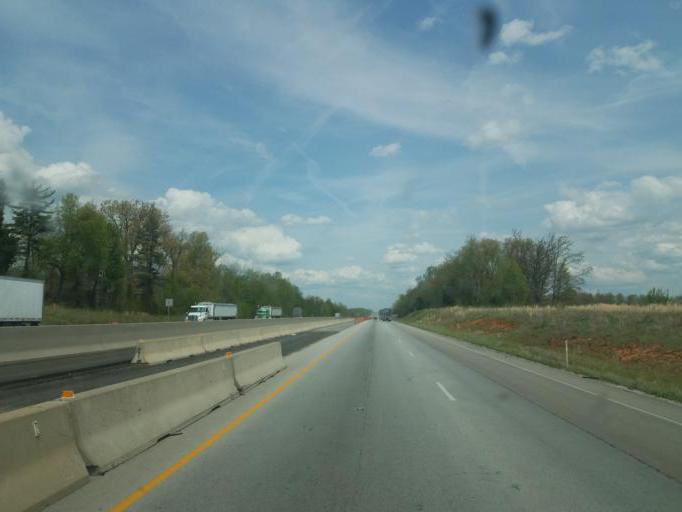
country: US
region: Kentucky
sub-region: Hardin County
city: Elizabethtown
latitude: 37.6125
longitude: -85.8651
